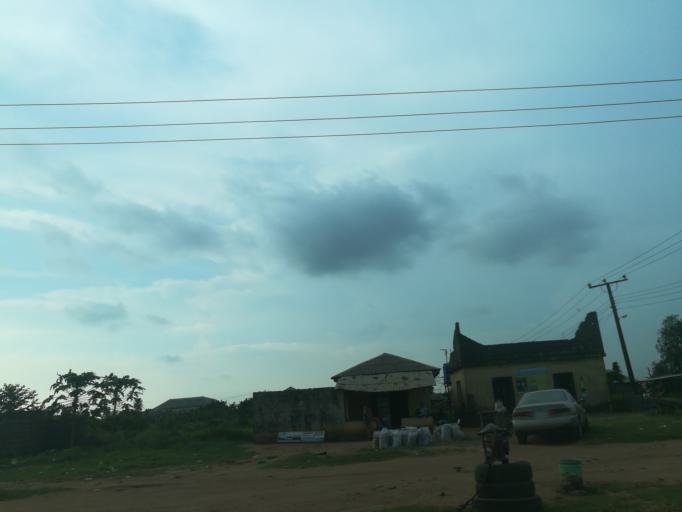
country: NG
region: Lagos
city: Ikorodu
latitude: 6.6096
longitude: 3.5942
